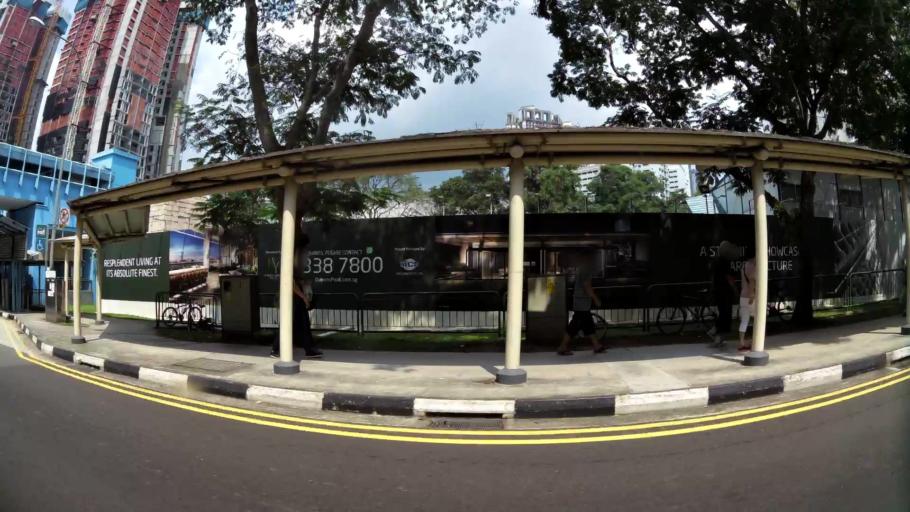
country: SG
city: Singapore
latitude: 1.2941
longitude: 103.8067
